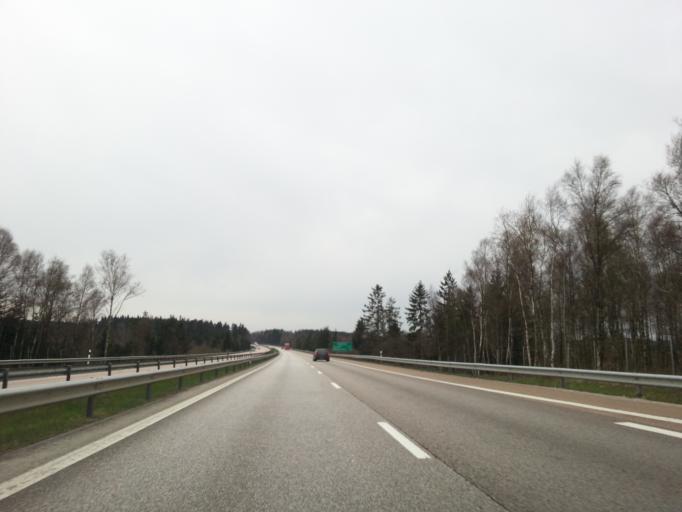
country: SE
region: Skane
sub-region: Bastads Kommun
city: Bastad
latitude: 56.3828
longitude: 12.9360
